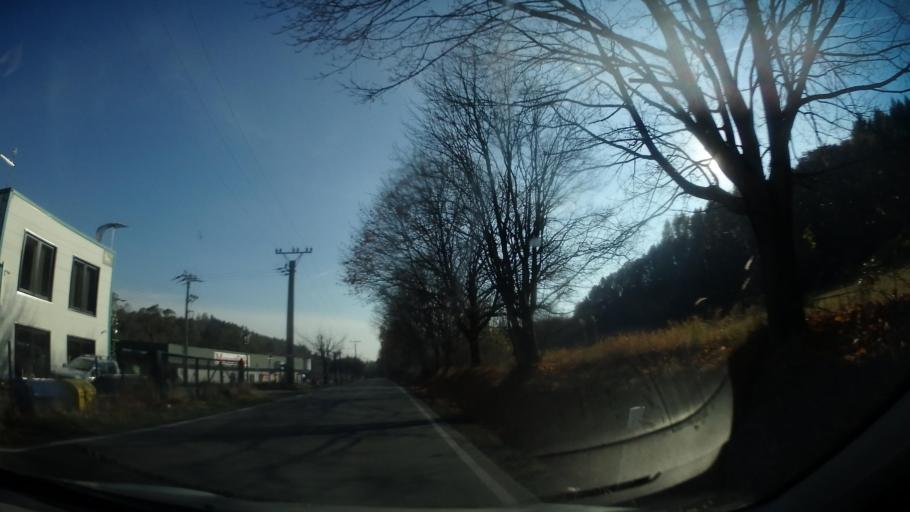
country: CZ
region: Central Bohemia
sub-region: Okres Praha-Vychod
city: Mnichovice
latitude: 49.9261
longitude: 14.7172
